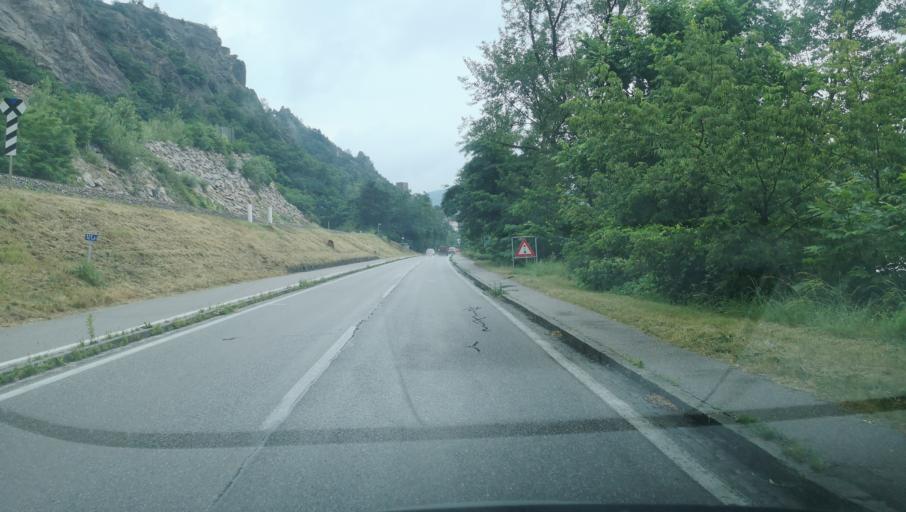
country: AT
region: Lower Austria
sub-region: Politischer Bezirk Krems
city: Durnstein
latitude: 48.4019
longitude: 15.5167
